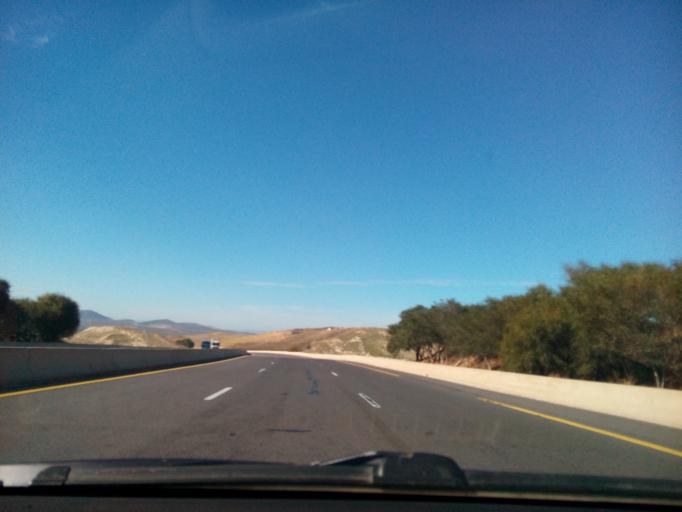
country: DZ
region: Tlemcen
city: Ouled Mimoun
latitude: 35.0296
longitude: -0.9884
